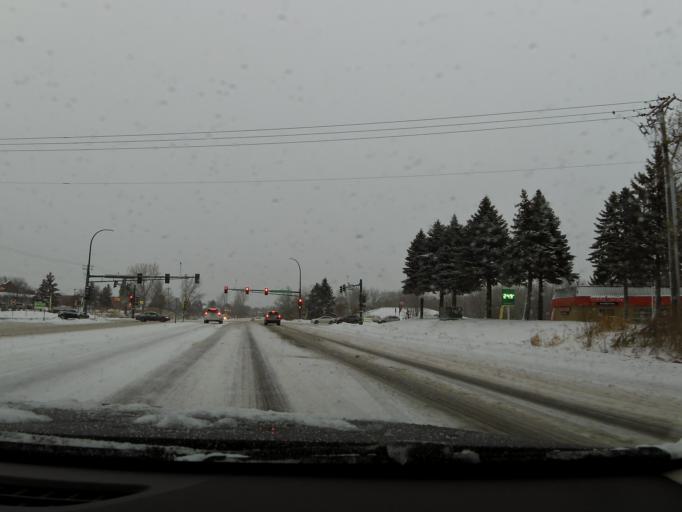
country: US
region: Minnesota
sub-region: Hennepin County
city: Eden Prairie
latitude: 44.8478
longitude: -93.4397
